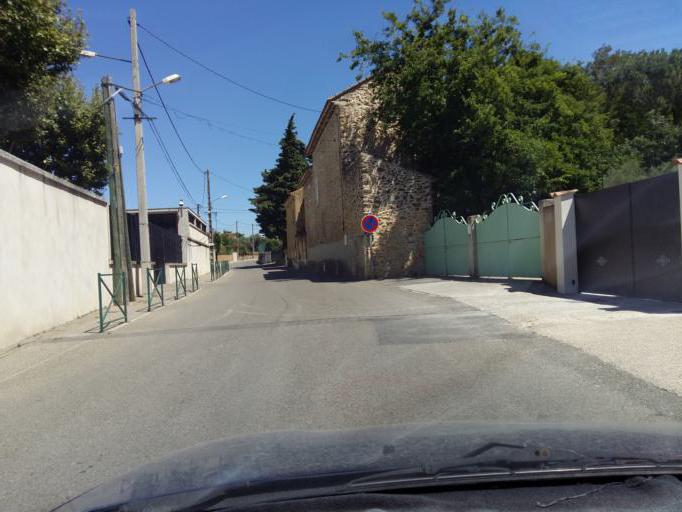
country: FR
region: Provence-Alpes-Cote d'Azur
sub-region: Departement du Vaucluse
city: Piolenc
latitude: 44.1771
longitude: 4.7639
